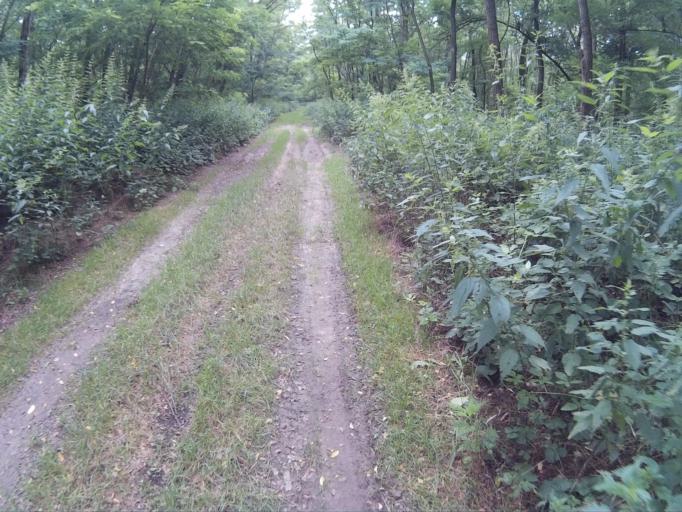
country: HU
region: Veszprem
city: Papa
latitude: 47.2801
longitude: 17.5669
